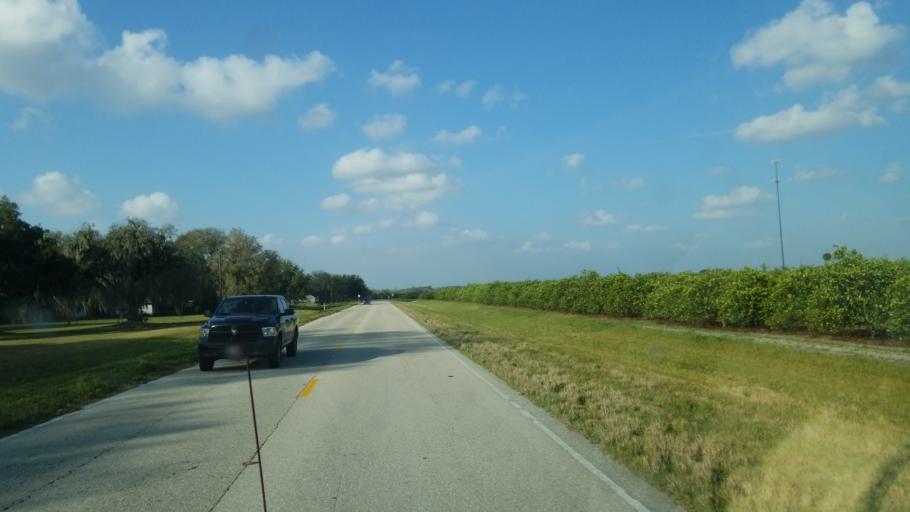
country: US
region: Florida
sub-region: Hardee County
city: Bowling Green
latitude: 27.5886
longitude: -81.9364
